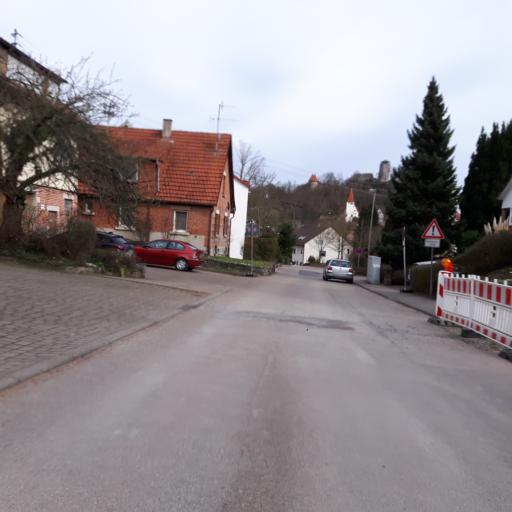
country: DE
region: Baden-Wuerttemberg
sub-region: Regierungsbezirk Stuttgart
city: Beilstein
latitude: 49.0425
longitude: 9.3086
